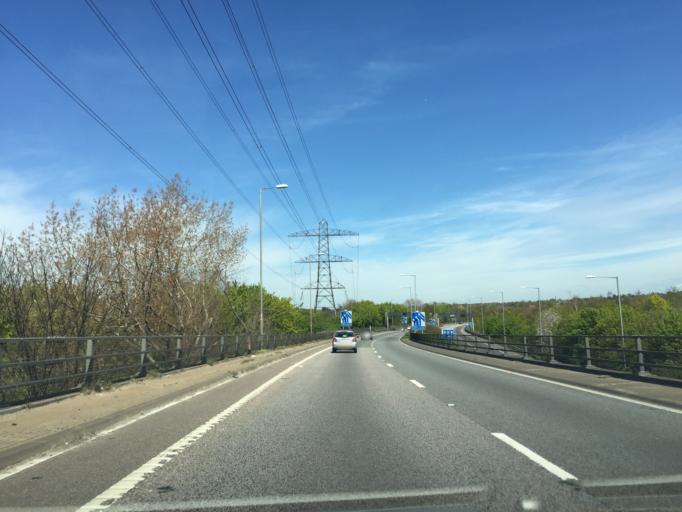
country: GB
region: England
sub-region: Greater London
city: Woodford Green
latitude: 51.5950
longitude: 0.0393
